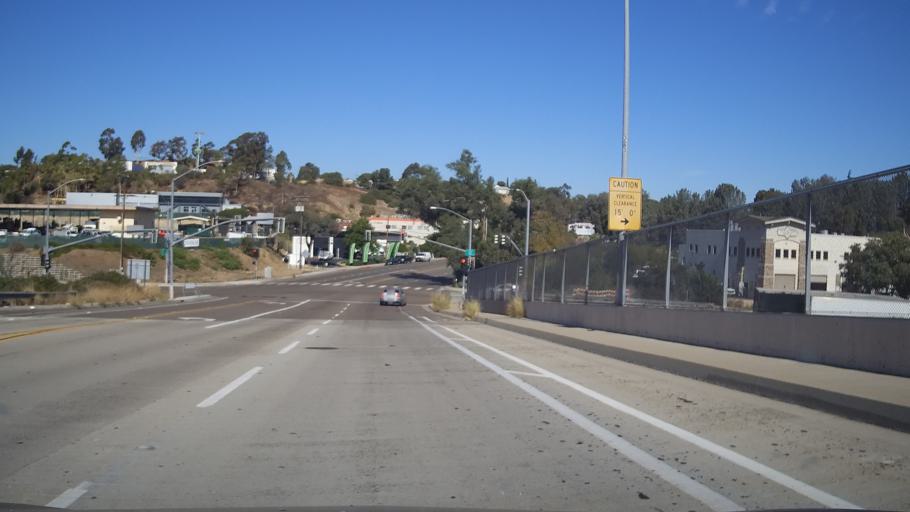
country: US
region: California
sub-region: San Diego County
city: National City
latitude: 32.7187
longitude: -117.1104
